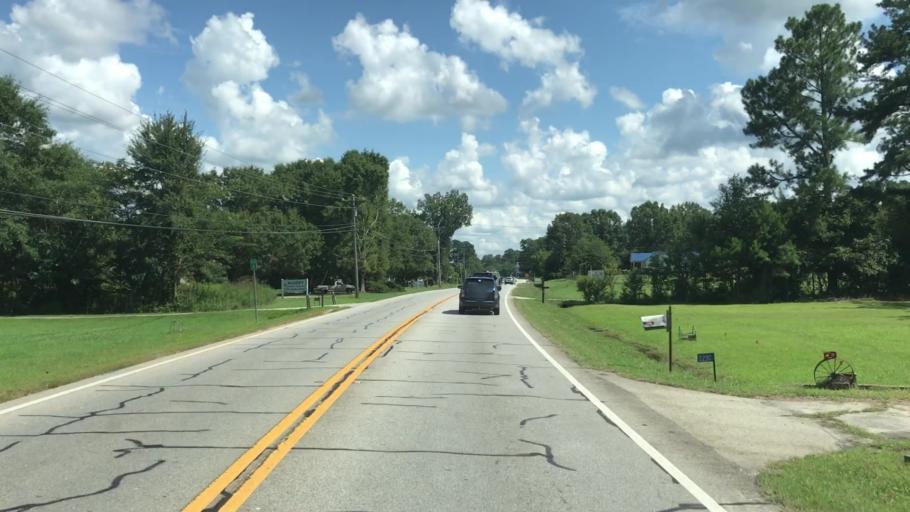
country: US
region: Georgia
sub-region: Walton County
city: Walnut Grove
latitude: 33.7898
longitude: -83.8586
